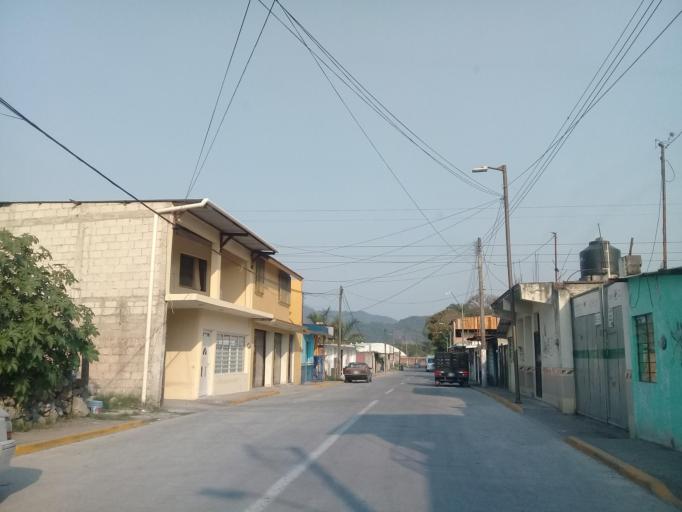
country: MX
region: Veracruz
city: Ixtac Zoquitlan
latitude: 18.8548
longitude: -97.0540
